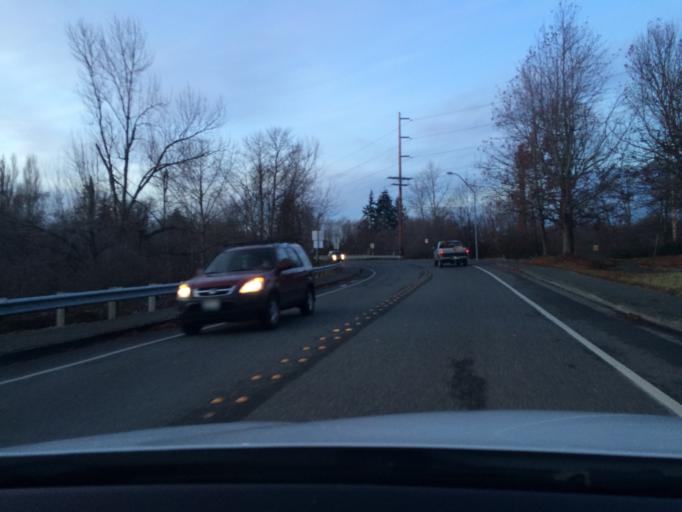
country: US
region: Washington
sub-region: Whatcom County
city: Bellingham
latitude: 48.7653
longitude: -122.5152
